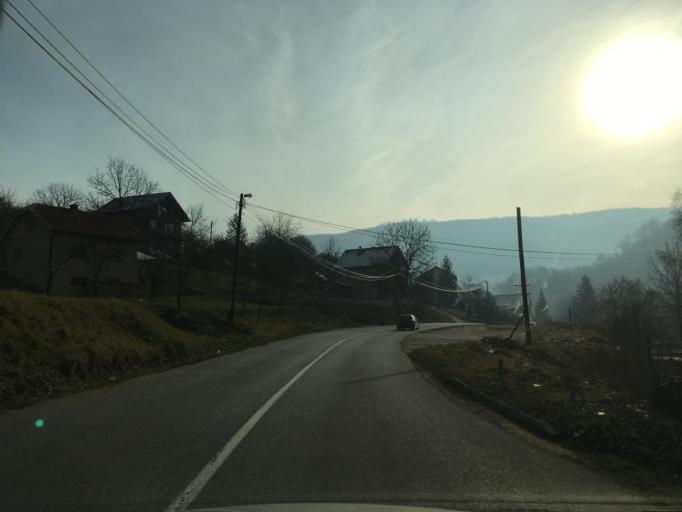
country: BA
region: Federation of Bosnia and Herzegovina
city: Lokvine
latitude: 44.1904
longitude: 17.8583
